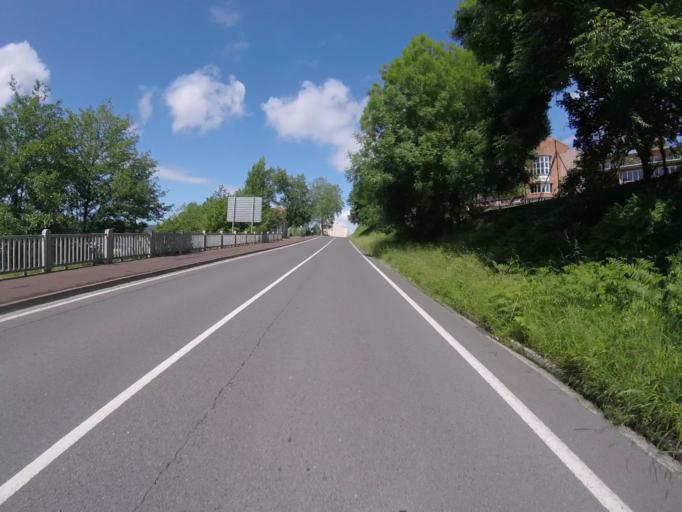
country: ES
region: Basque Country
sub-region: Provincia de Guipuzcoa
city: Errenteria
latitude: 43.2921
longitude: -1.8999
